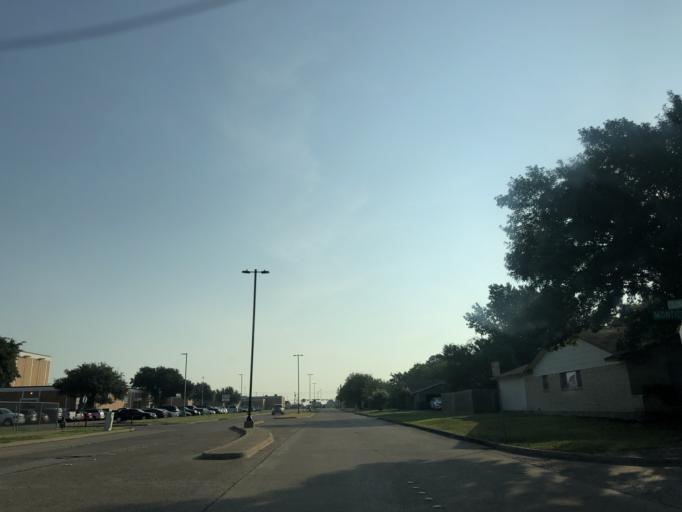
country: US
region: Texas
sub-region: Dallas County
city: Garland
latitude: 32.8711
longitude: -96.6190
